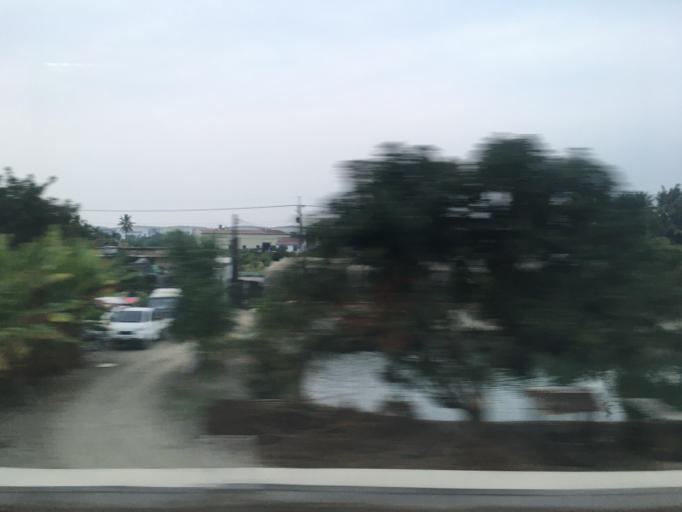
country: TW
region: Taiwan
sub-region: Pingtung
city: Pingtung
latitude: 22.6634
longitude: 120.4561
